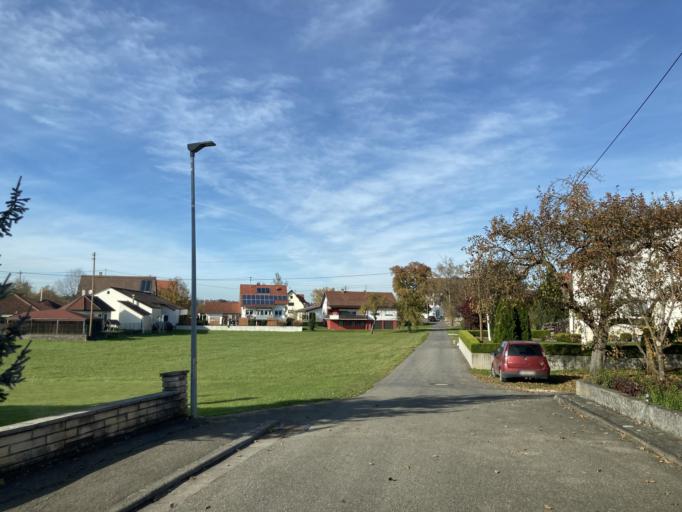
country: DE
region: Baden-Wuerttemberg
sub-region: Tuebingen Region
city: Hirrlingen
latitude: 48.4184
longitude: 8.9229
